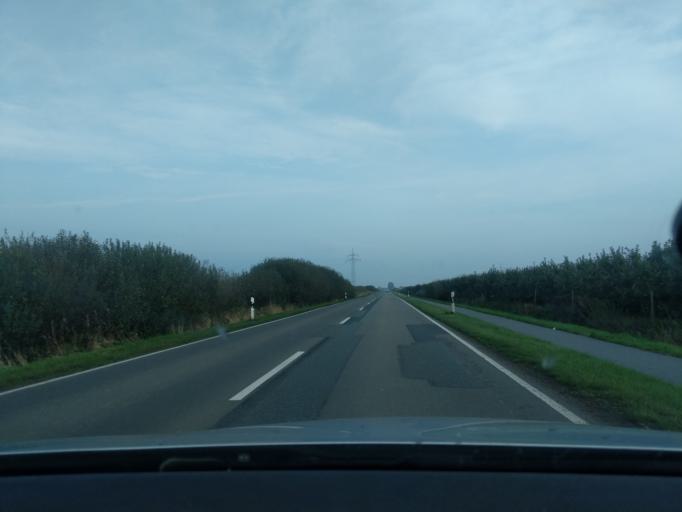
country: DE
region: Lower Saxony
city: Guderhandviertel
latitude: 53.5460
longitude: 9.5788
